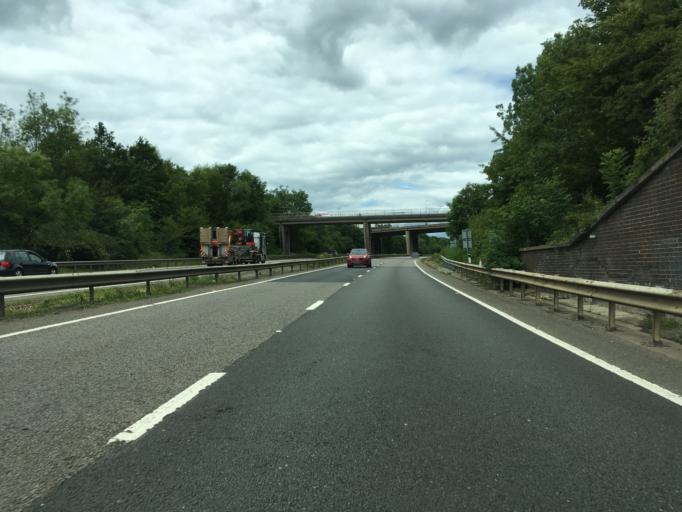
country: GB
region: England
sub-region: Buckinghamshire
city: Bletchley
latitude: 52.0125
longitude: -0.7468
